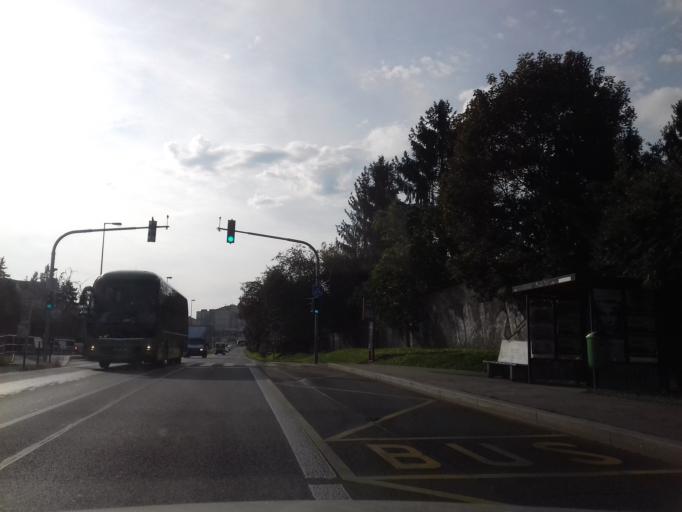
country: CZ
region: Praha
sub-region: Praha 4
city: Hodkovicky
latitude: 50.0247
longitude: 14.4599
